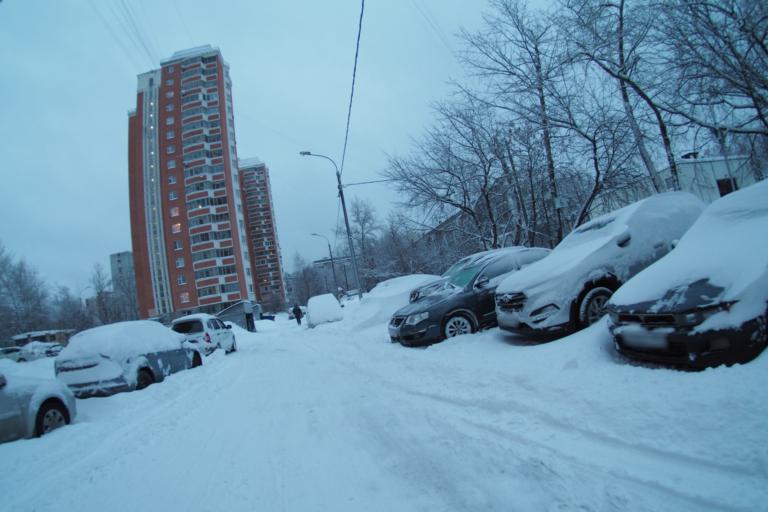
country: RU
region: Moscow
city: Ryazanskiy
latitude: 55.7437
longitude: 37.7775
